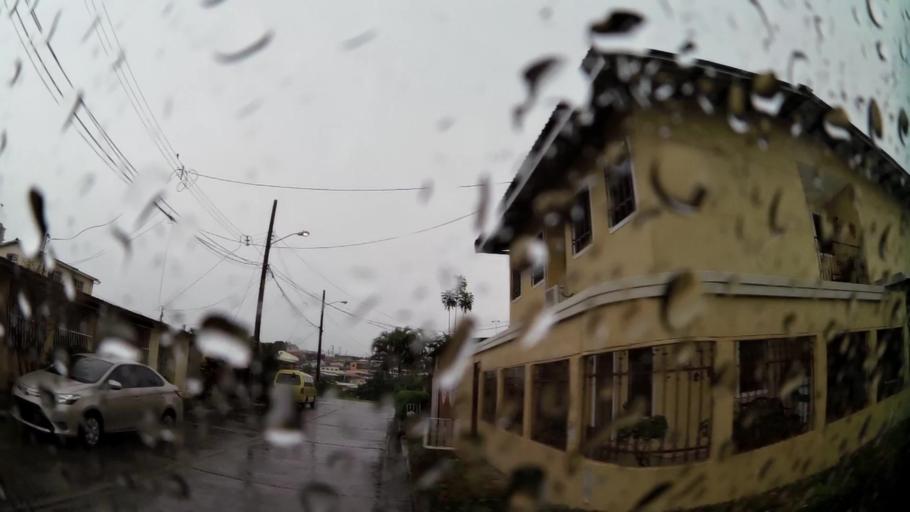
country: PA
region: Panama
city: San Miguelito
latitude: 9.0514
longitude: -79.4729
